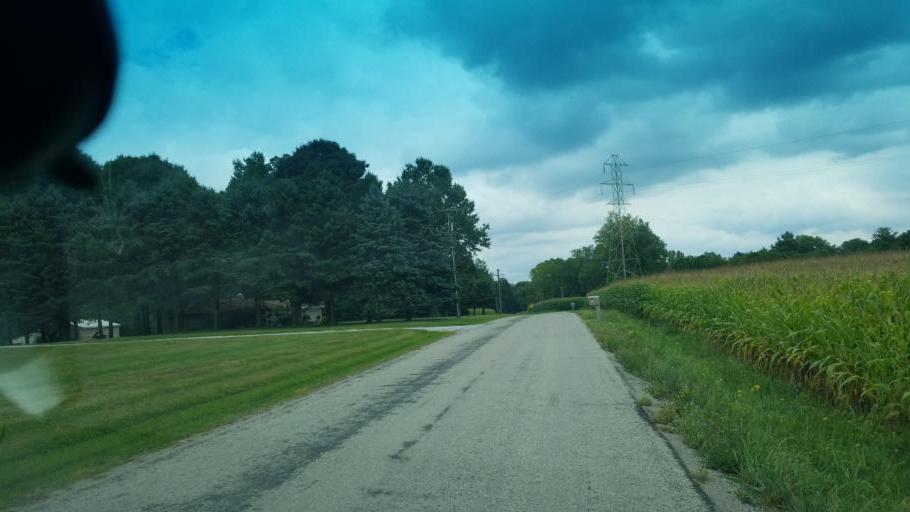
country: US
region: Ohio
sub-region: Richland County
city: Mansfield
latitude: 40.8493
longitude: -82.5398
